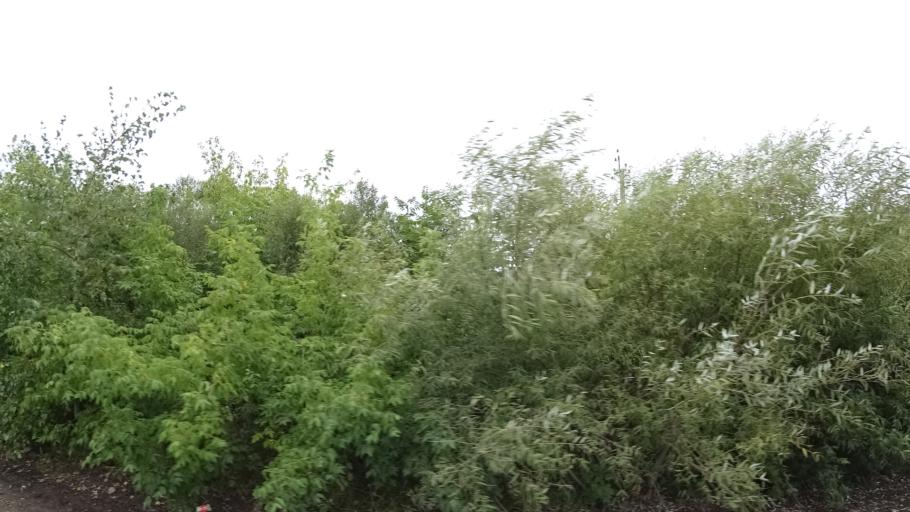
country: RU
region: Primorskiy
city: Chernigovka
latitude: 44.3358
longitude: 132.5616
